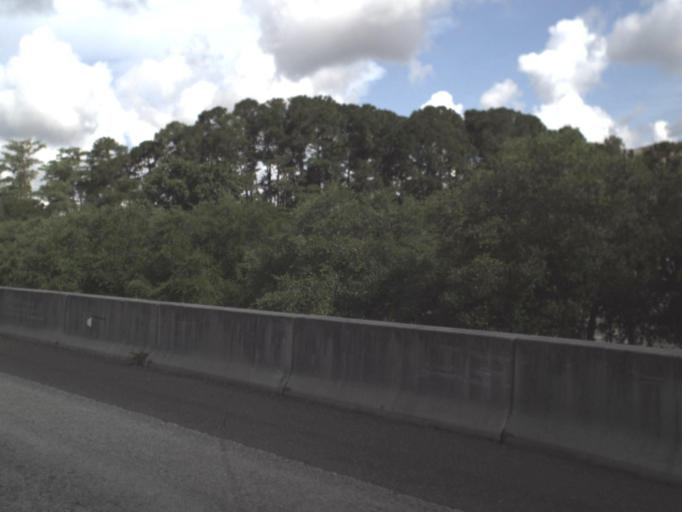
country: US
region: Florida
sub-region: Duval County
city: Jacksonville
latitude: 30.2513
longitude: -81.5812
